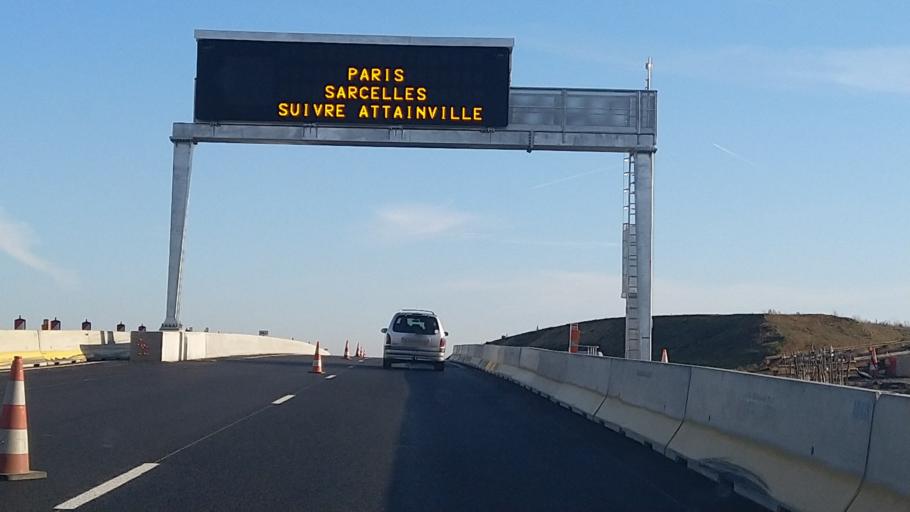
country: FR
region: Ile-de-France
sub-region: Departement du Val-d'Oise
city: Maffliers
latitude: 49.0896
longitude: 2.3094
